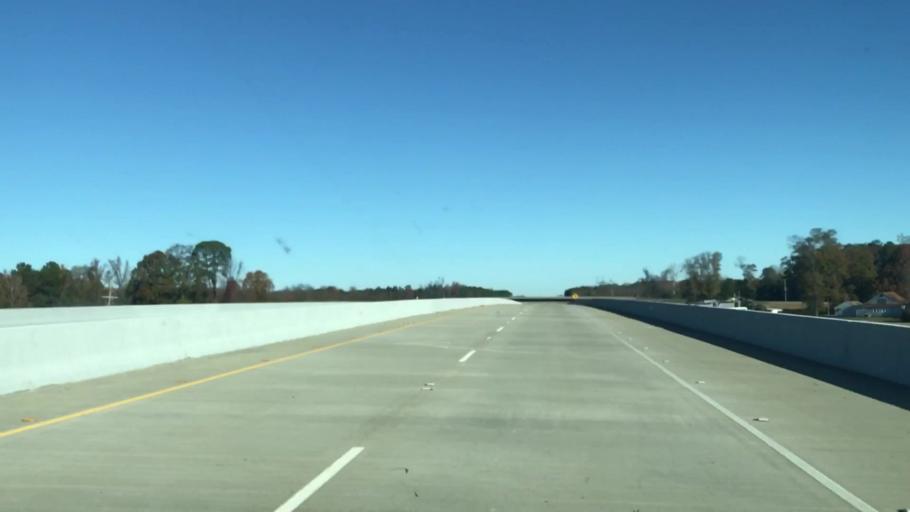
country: US
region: Louisiana
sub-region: Caddo Parish
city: Blanchard
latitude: 32.5960
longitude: -93.8315
